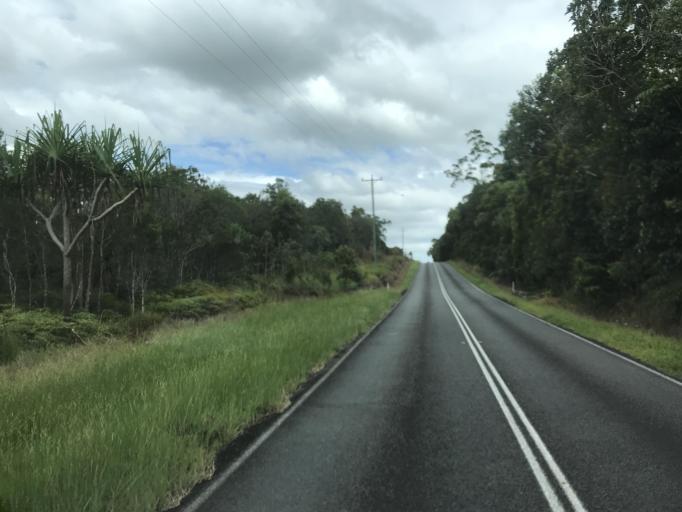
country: AU
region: Queensland
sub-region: Cassowary Coast
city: Innisfail
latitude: -17.8444
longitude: 146.0564
